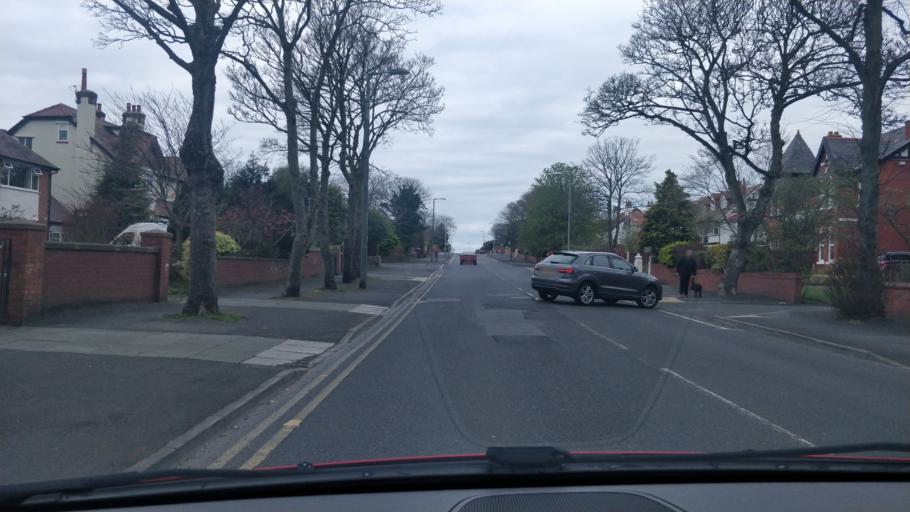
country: GB
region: England
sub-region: Sefton
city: Formby
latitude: 53.6026
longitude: -3.0437
